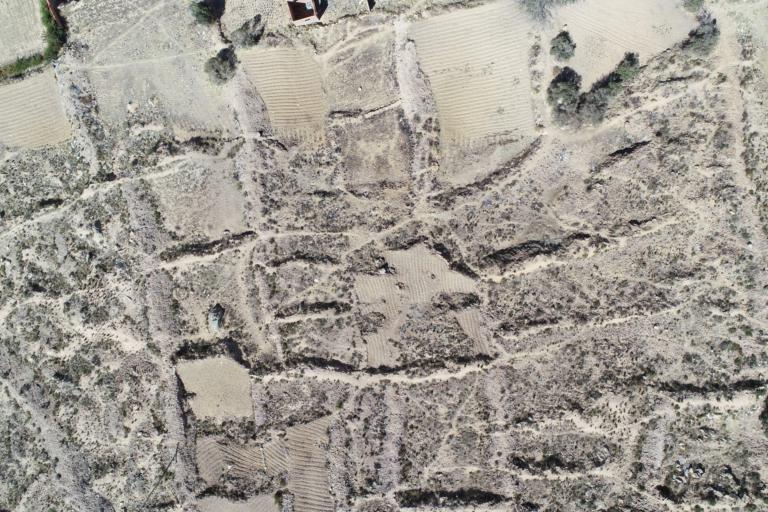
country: BO
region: La Paz
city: Achacachi
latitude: -16.0463
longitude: -68.6784
